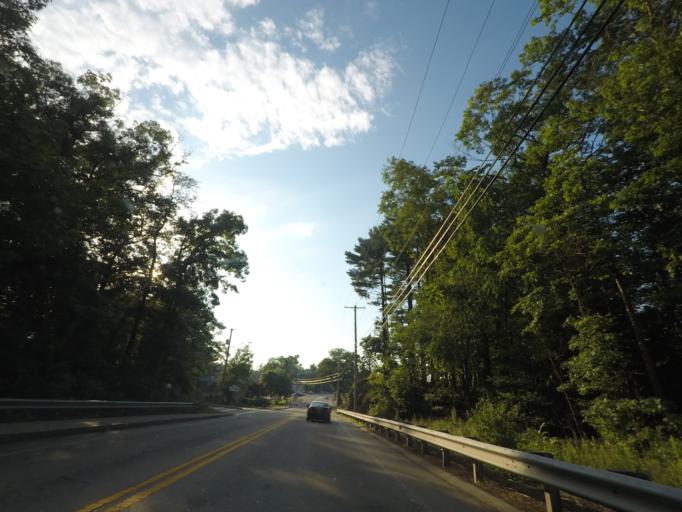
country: US
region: Massachusetts
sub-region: Worcester County
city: Sturbridge
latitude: 42.0950
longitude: -72.0703
